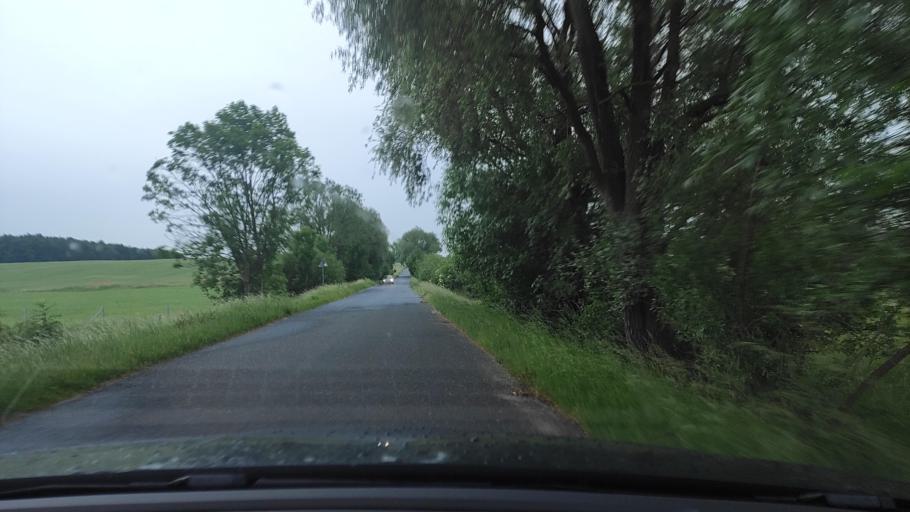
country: PL
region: Greater Poland Voivodeship
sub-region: Powiat poznanski
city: Kobylnica
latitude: 52.4939
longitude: 17.1300
